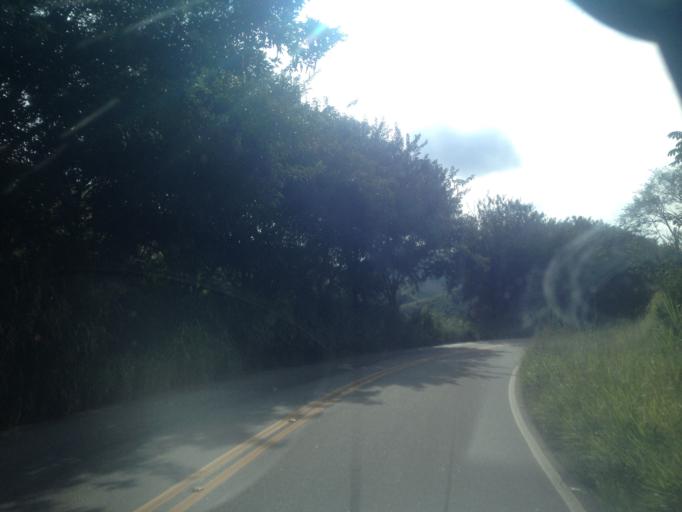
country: BR
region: Rio de Janeiro
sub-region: Quatis
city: Quatis
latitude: -22.3443
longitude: -44.2449
